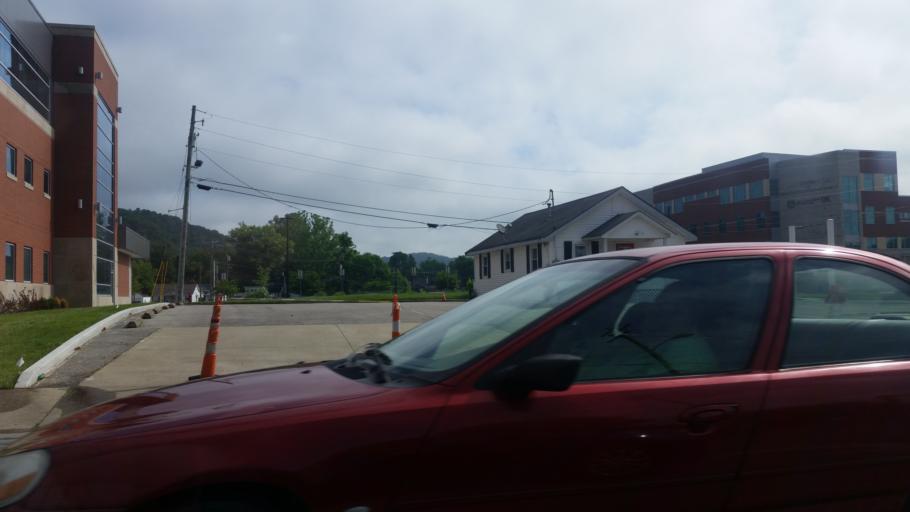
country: US
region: Kentucky
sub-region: Rowan County
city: Morehead
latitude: 38.1789
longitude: -83.4408
